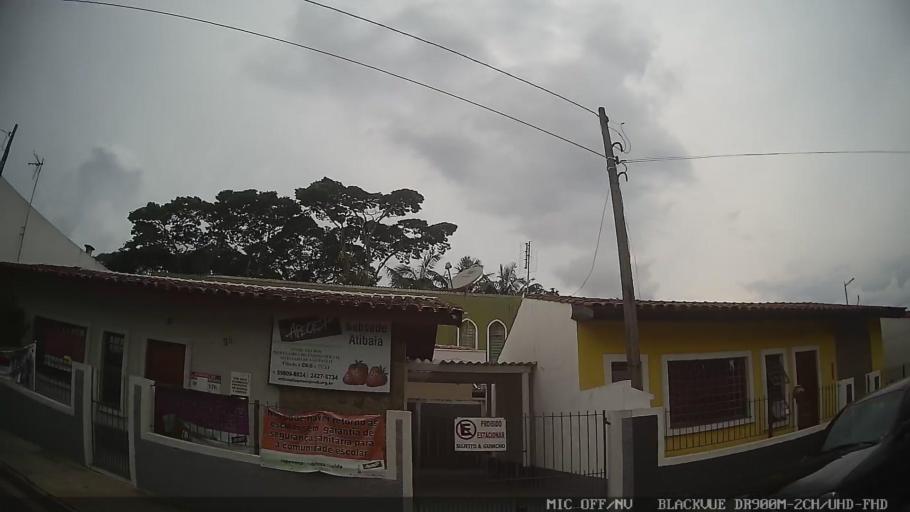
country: BR
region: Sao Paulo
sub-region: Atibaia
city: Atibaia
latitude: -23.1249
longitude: -46.5648
